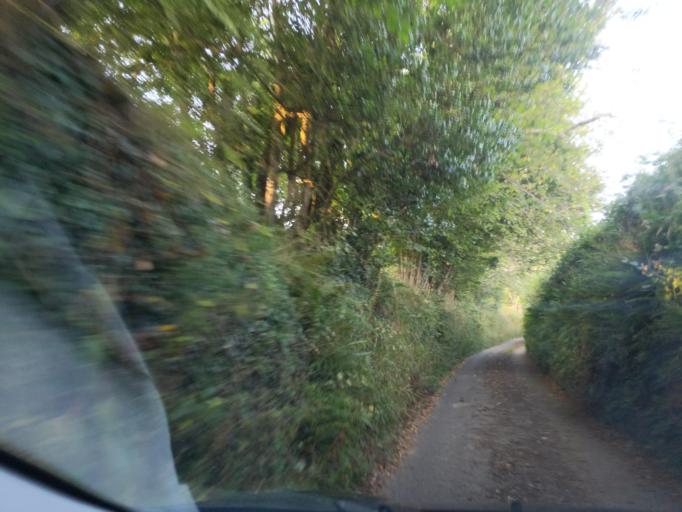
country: GB
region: England
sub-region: Cornwall
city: Fowey
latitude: 50.3659
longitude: -4.5933
